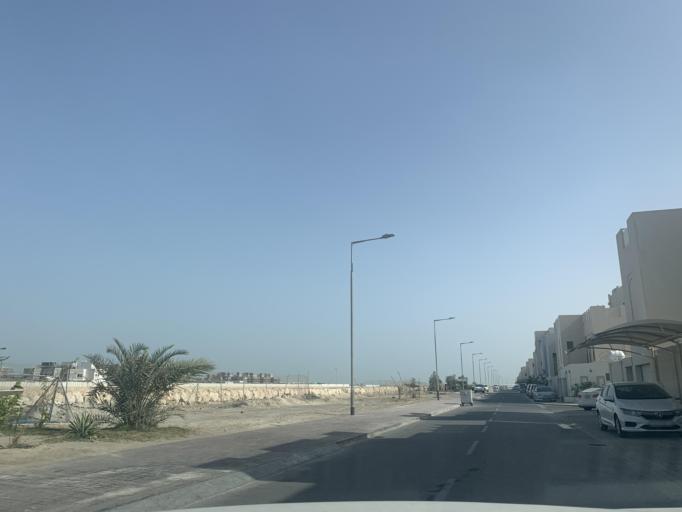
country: BH
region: Northern
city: Sitrah
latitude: 26.1623
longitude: 50.6293
